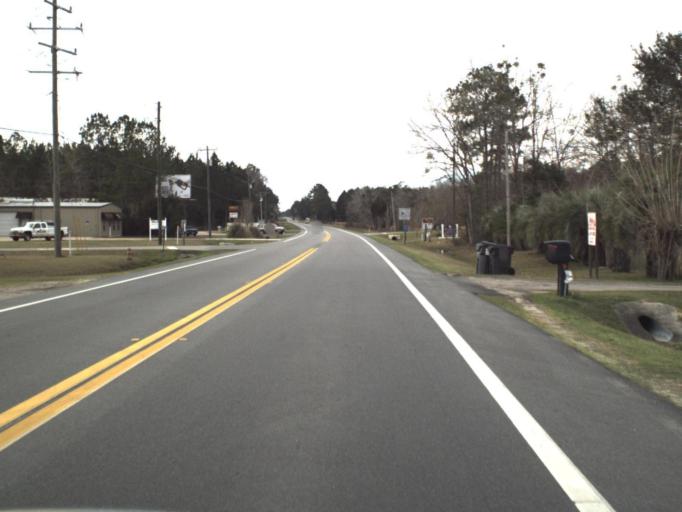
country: US
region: Florida
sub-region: Gulf County
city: Wewahitchka
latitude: 30.1177
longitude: -85.2089
